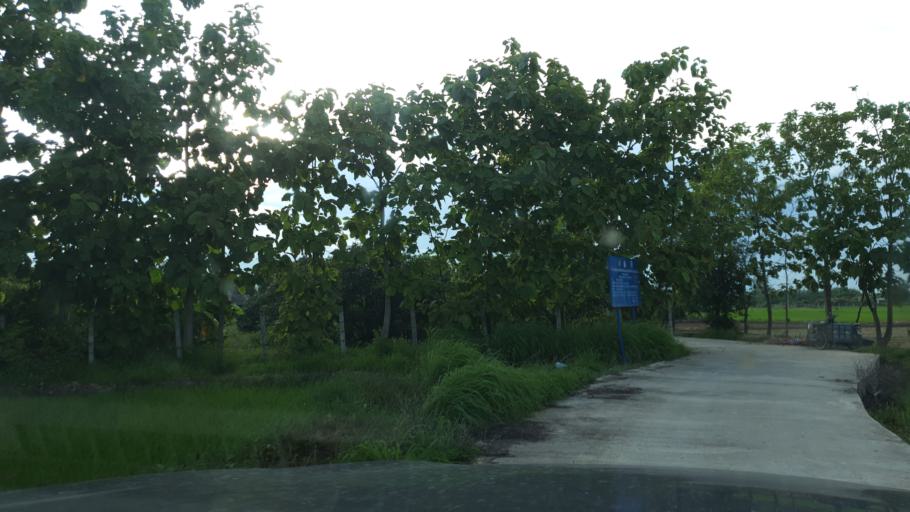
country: TH
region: Lamphun
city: Ban Thi
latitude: 18.6440
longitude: 99.1043
